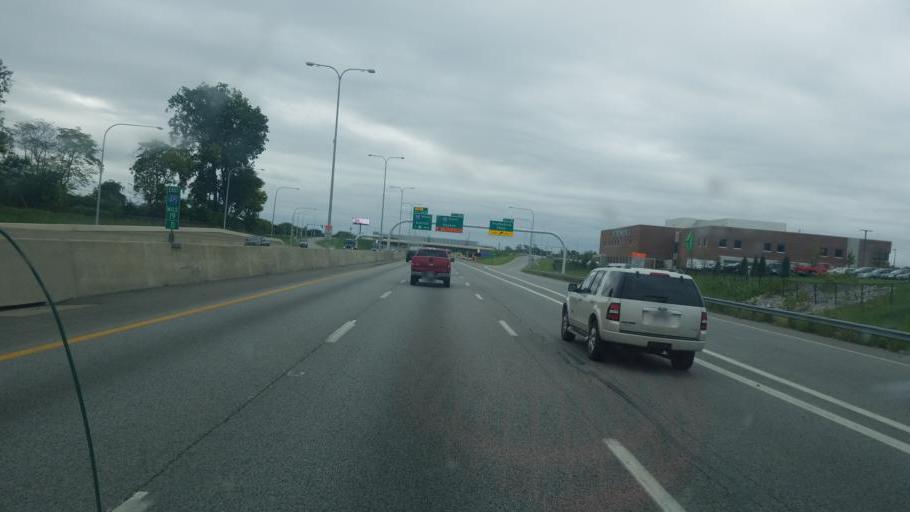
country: US
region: Ohio
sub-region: Lucas County
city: Toledo
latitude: 41.6816
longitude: -83.5956
